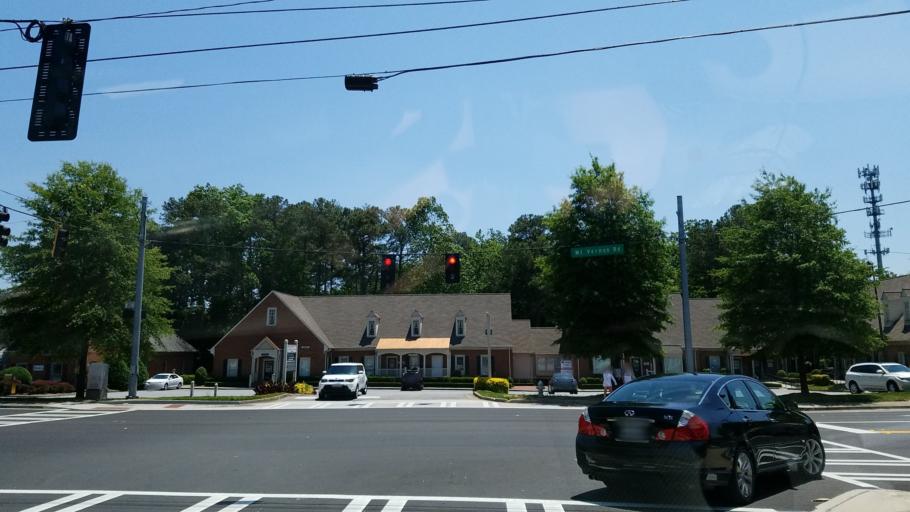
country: US
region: Georgia
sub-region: DeKalb County
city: Dunwoody
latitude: 33.9471
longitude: -84.3316
